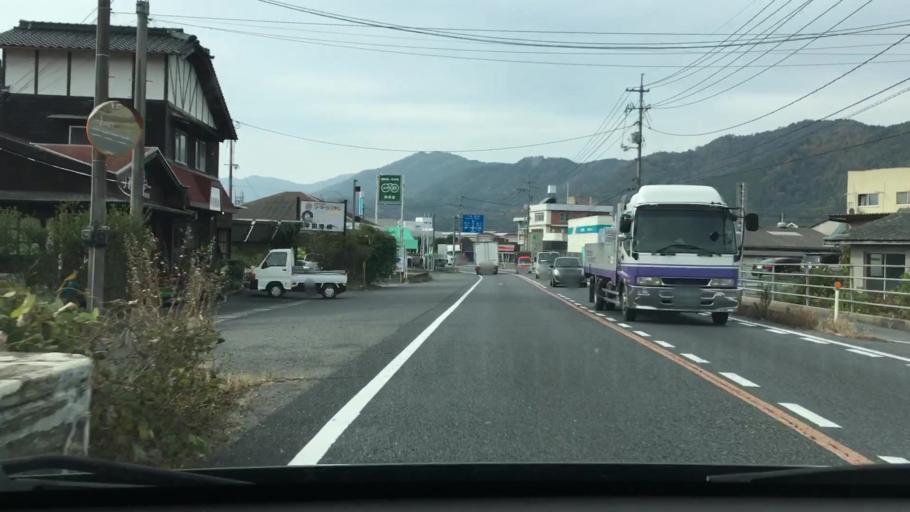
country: JP
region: Yamaguchi
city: Yanai
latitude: 34.0923
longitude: 132.0554
